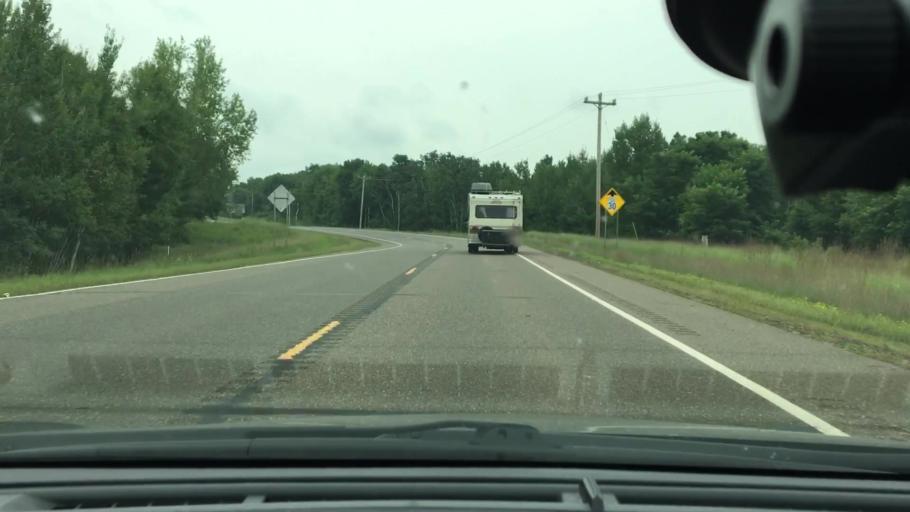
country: US
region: Minnesota
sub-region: Crow Wing County
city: Crosby
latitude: 46.4903
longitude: -93.9571
